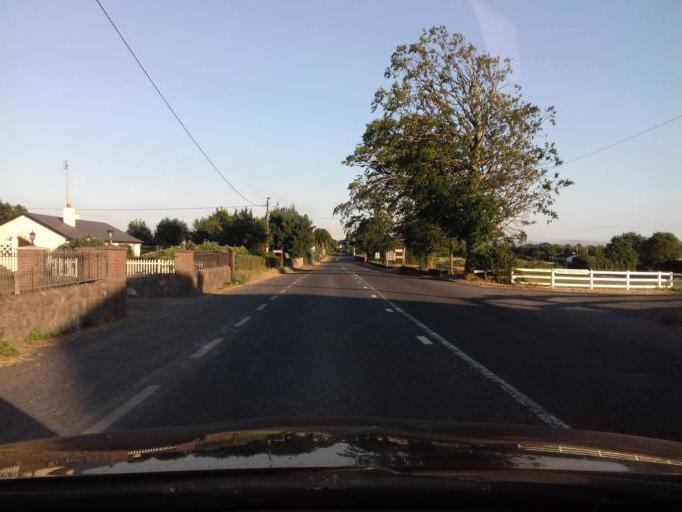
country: IE
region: Leinster
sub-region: Dublin City
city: Finglas
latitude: 53.4382
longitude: -6.3362
